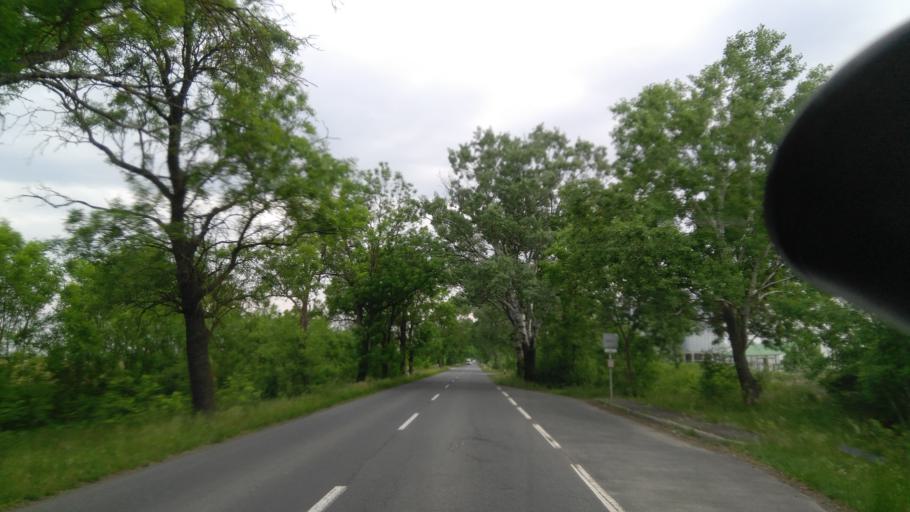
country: HU
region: Bekes
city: Veszto
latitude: 46.8922
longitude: 21.2453
